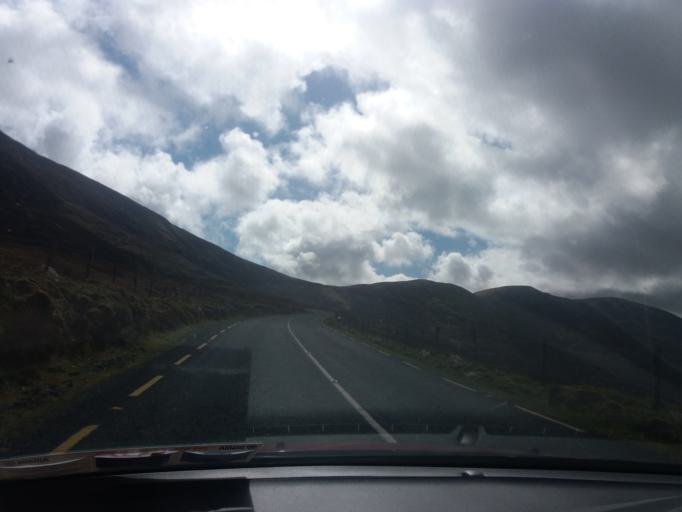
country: IE
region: Munster
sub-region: Ciarrai
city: Dingle
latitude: 52.1906
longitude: -10.1899
